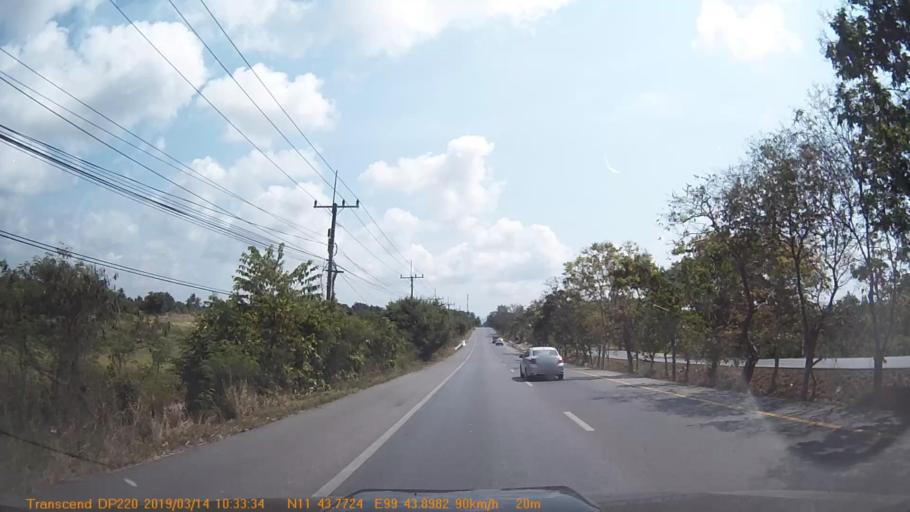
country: TH
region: Prachuap Khiri Khan
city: Prachuap Khiri Khan
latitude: 11.7204
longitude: 99.7236
